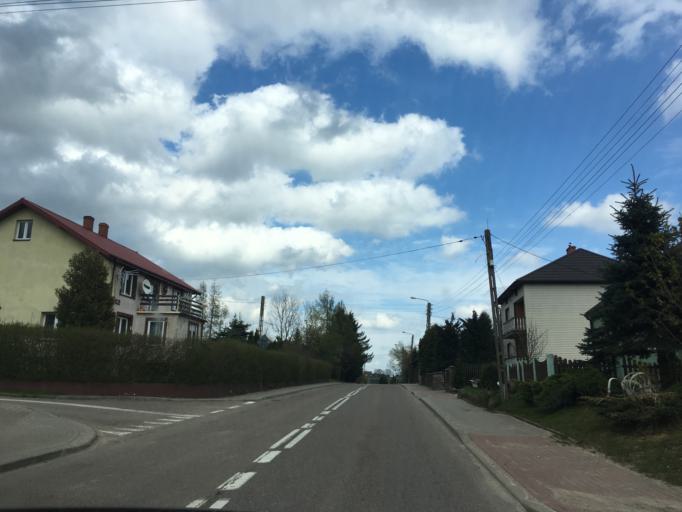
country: PL
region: Podlasie
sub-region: Suwalki
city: Suwalki
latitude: 54.3636
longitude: 22.8621
